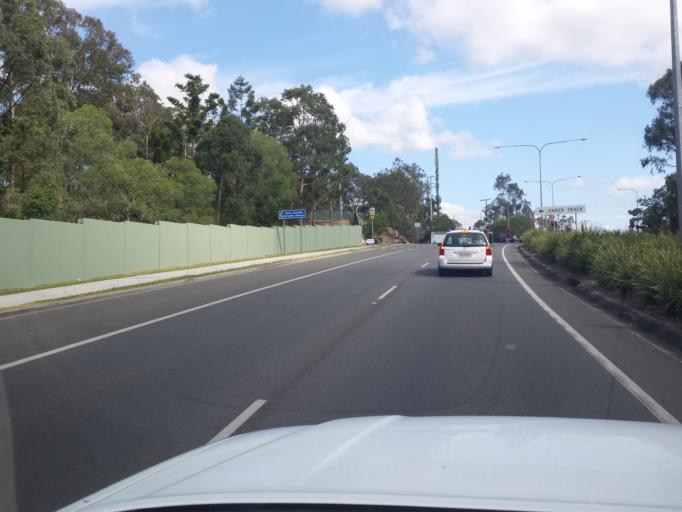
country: AU
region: Queensland
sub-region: Brisbane
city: Bridegman Downs
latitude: -27.3654
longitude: 152.9751
